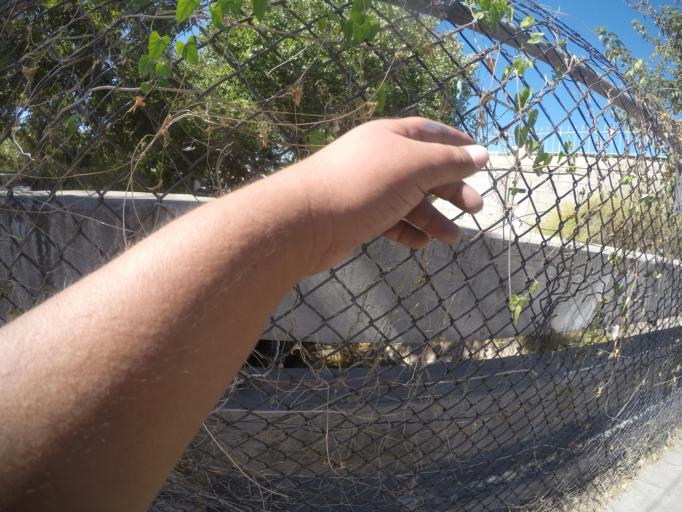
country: MX
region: Chihuahua
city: Ciudad Juarez
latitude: 31.7395
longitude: -106.4699
